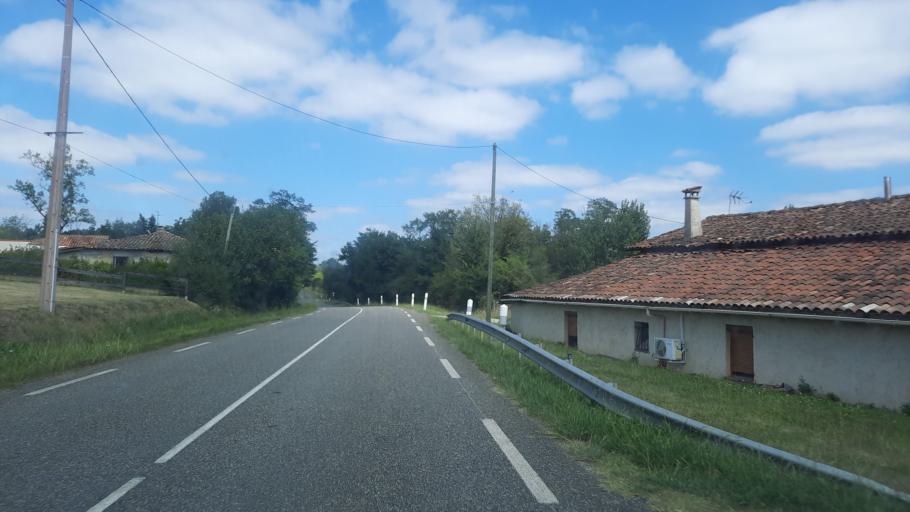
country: FR
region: Midi-Pyrenees
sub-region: Departement du Gers
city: Lombez
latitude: 43.3906
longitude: 0.7831
